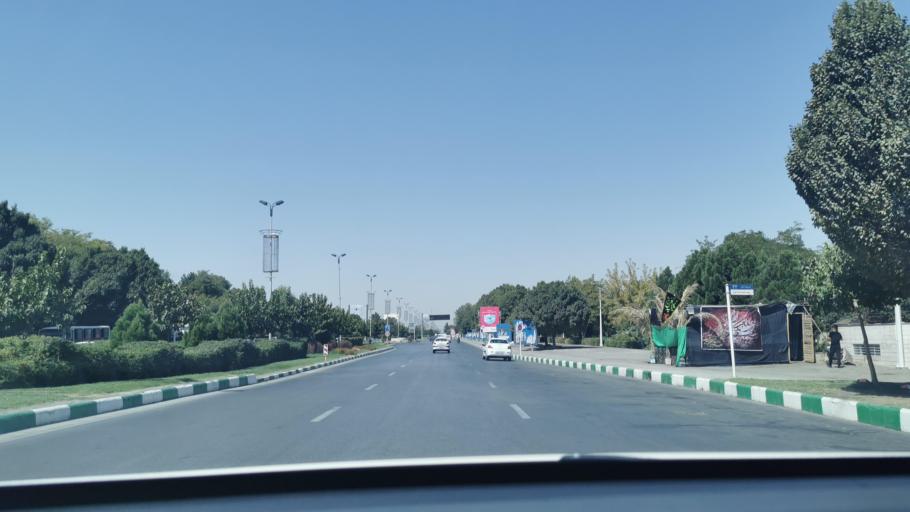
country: IR
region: Razavi Khorasan
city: Mashhad
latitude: 36.2535
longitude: 59.6134
